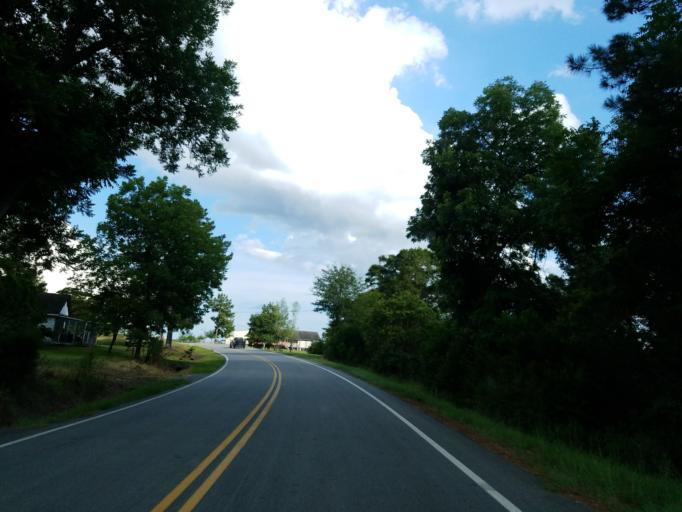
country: US
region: Georgia
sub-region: Crisp County
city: Cordele
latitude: 31.8276
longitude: -83.7396
